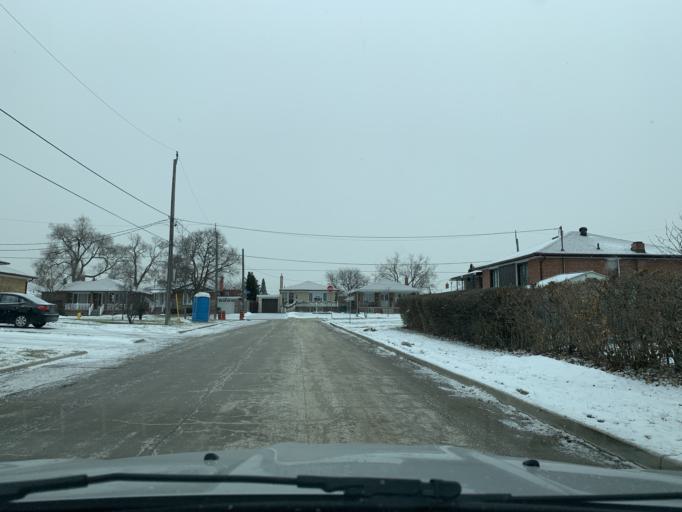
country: CA
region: Ontario
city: Concord
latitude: 43.7385
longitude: -79.4893
